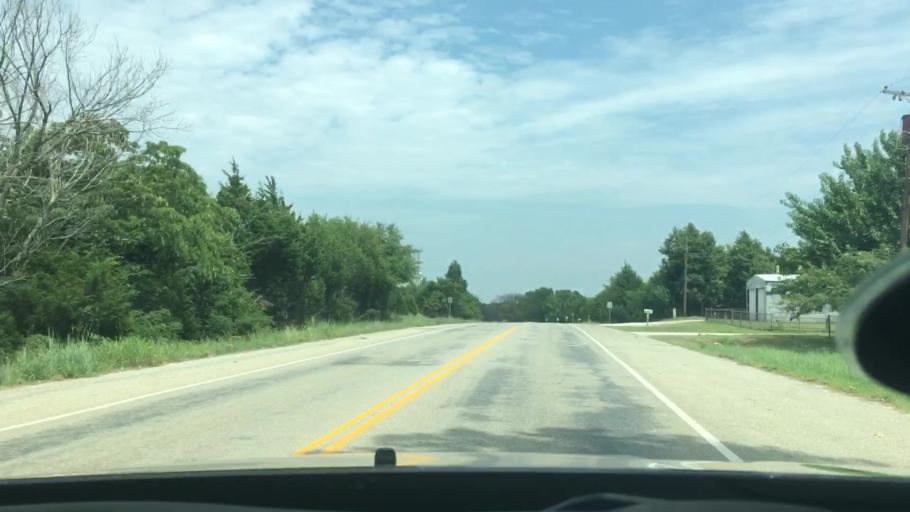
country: US
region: Oklahoma
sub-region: Pontotoc County
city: Byng
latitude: 34.8630
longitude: -96.6701
